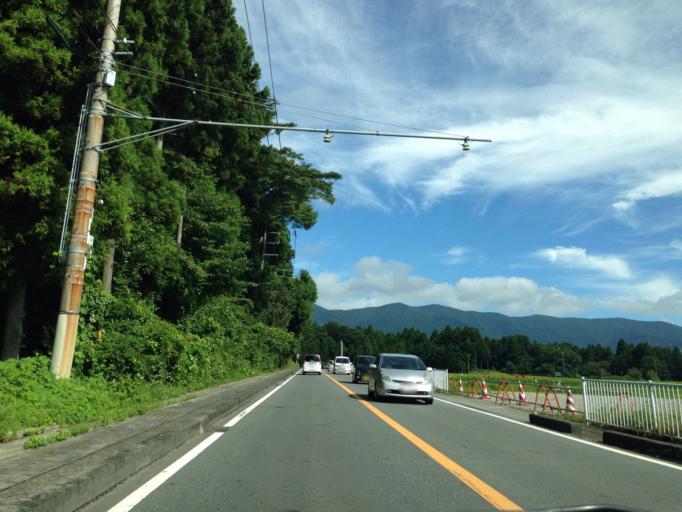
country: JP
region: Shizuoka
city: Gotemba
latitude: 35.3276
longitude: 138.9068
